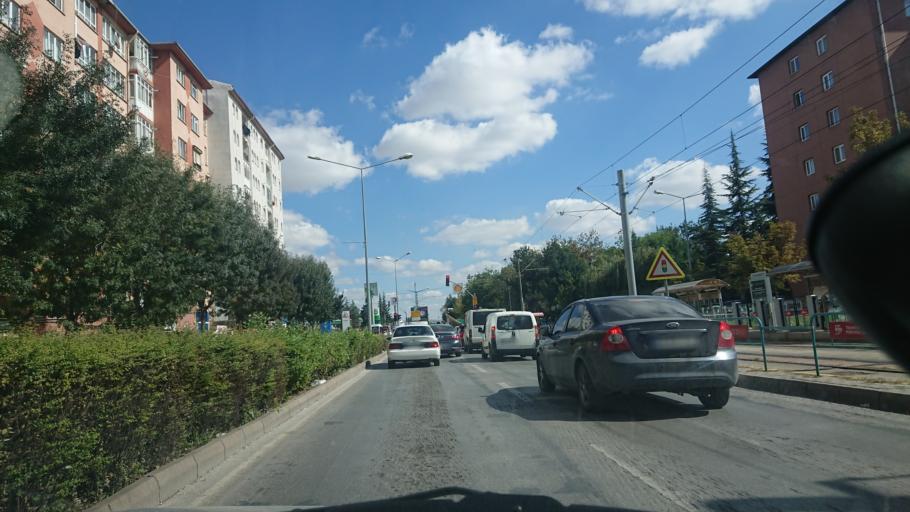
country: TR
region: Eskisehir
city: Eskisehir
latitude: 39.7644
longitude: 30.5549
